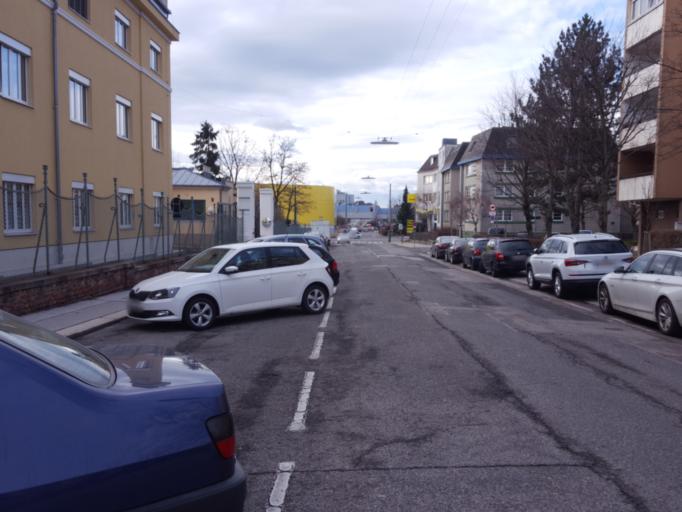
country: AT
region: Lower Austria
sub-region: Politischer Bezirk Modling
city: Vosendorf
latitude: 48.1735
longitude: 16.3200
